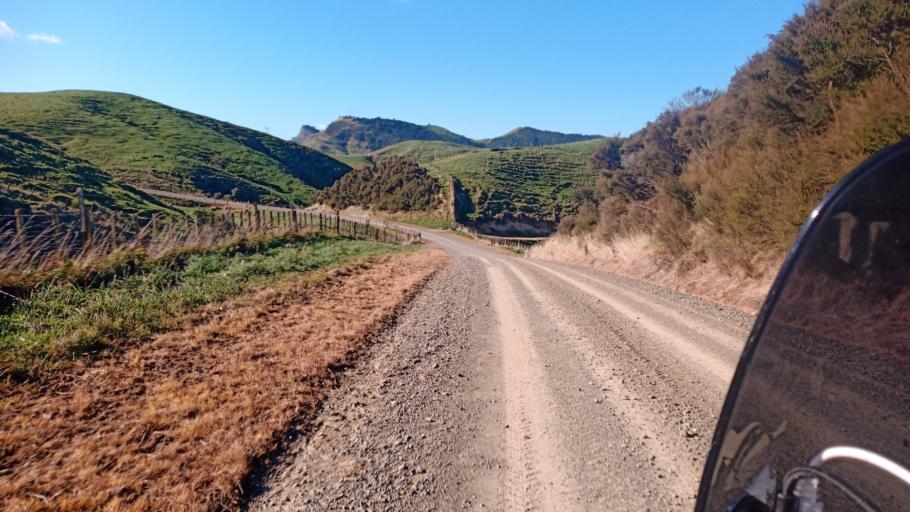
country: NZ
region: Hawke's Bay
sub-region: Wairoa District
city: Wairoa
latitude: -38.7485
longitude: 177.2756
